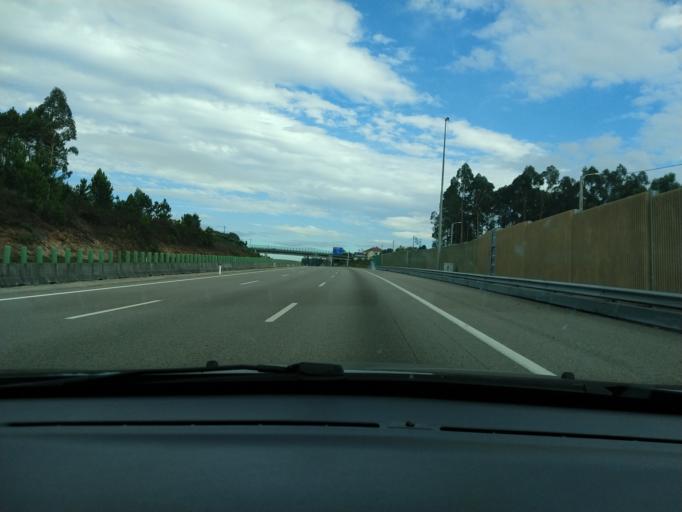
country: PT
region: Aveiro
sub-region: Santa Maria da Feira
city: Feira
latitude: 40.9031
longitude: -8.5667
